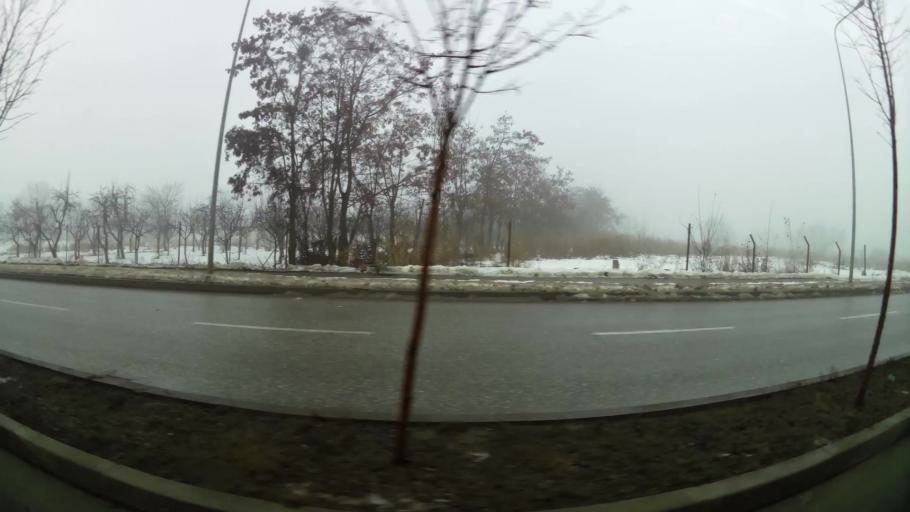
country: XK
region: Pristina
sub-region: Komuna e Prishtines
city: Pristina
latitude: 42.6492
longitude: 21.1489
